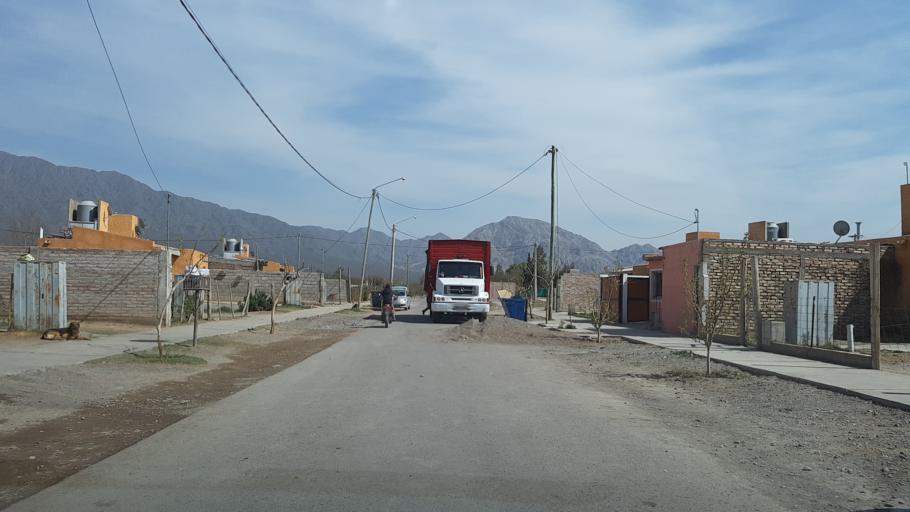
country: AR
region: San Juan
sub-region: Departamento de Zonda
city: Zonda
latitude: -31.5466
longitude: -68.7408
